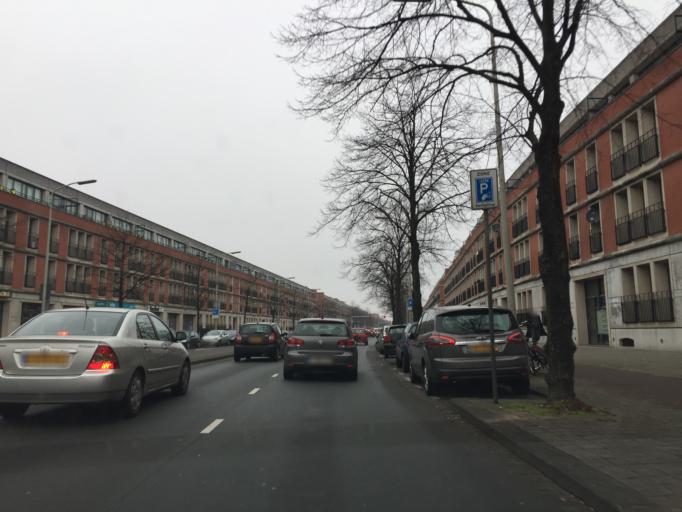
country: NL
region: South Holland
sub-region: Gemeente Den Haag
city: The Hague
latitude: 52.0660
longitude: 4.3051
